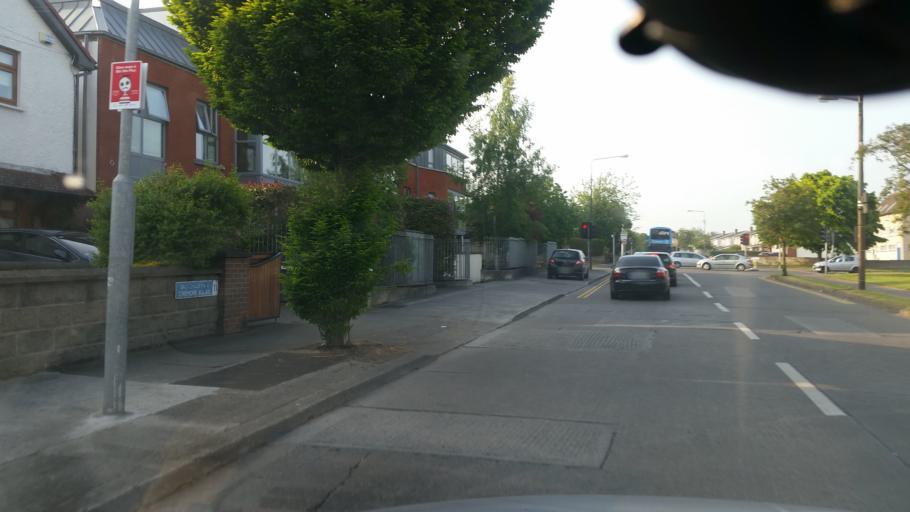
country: IE
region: Leinster
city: Glasnevin
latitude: 53.3790
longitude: -6.2764
